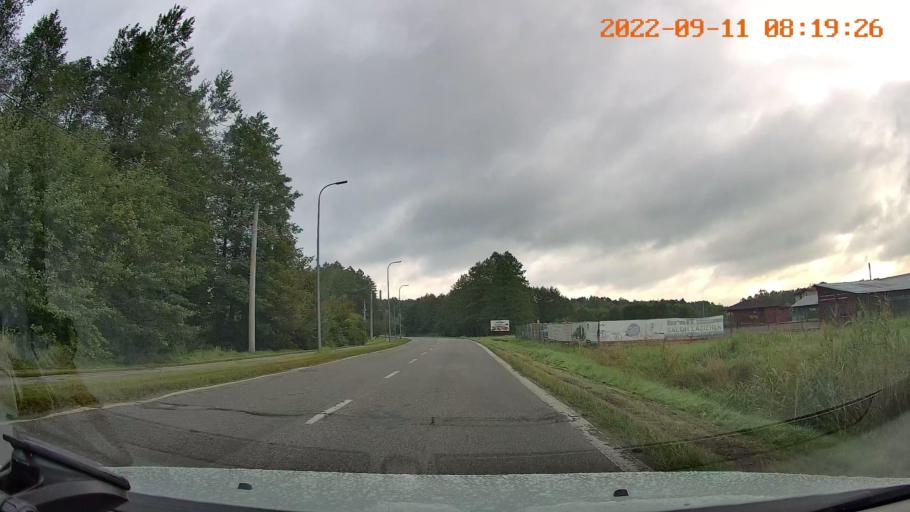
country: PL
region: Silesian Voivodeship
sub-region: Tychy
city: Tychy
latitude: 50.1515
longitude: 19.0056
